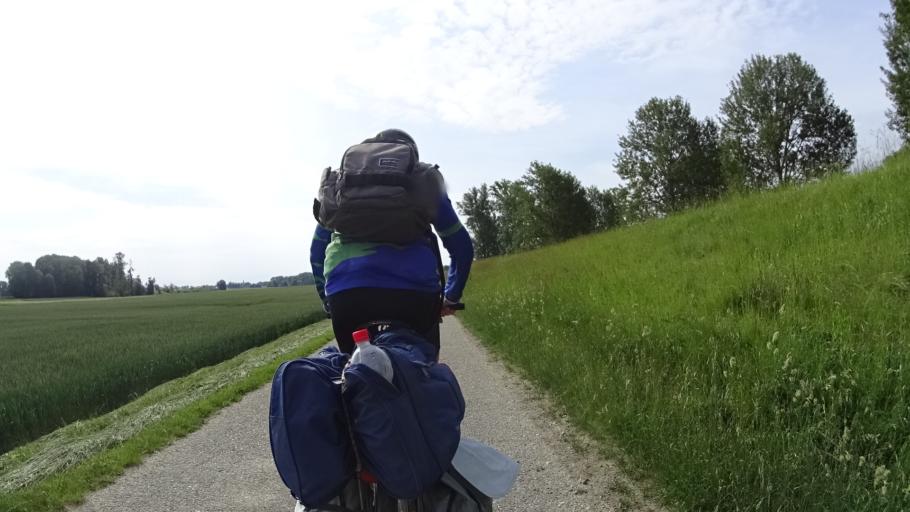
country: DE
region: Bavaria
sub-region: Lower Bavaria
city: Mariaposching
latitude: 48.8361
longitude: 12.7783
